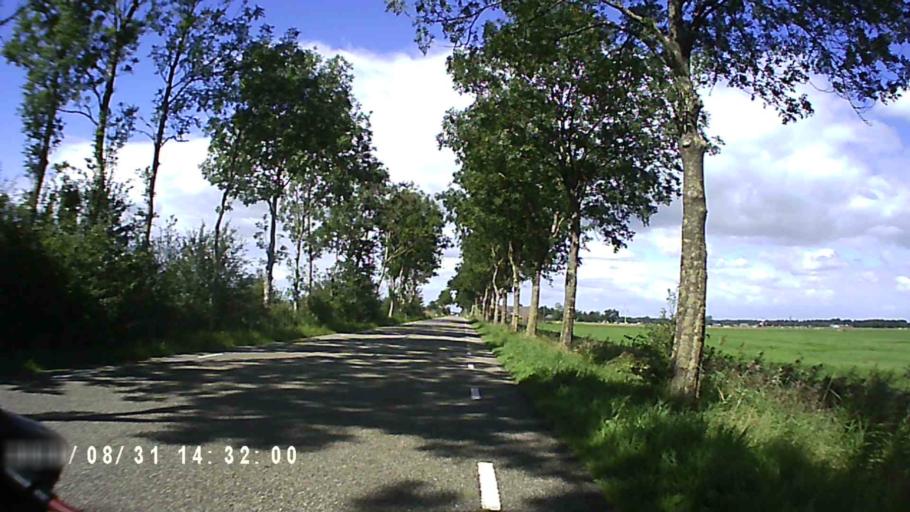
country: NL
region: Groningen
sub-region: Gemeente Zuidhorn
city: Zuidhorn
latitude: 53.2249
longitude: 6.4035
